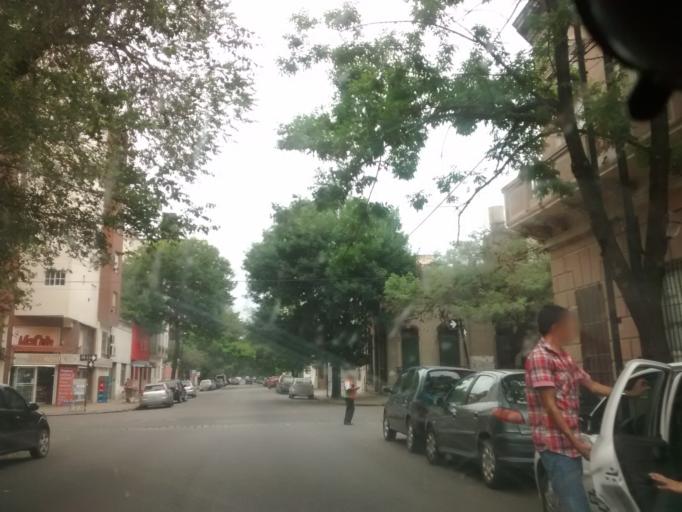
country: AR
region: Buenos Aires
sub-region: Partido de La Plata
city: La Plata
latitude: -34.9075
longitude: -57.9482
